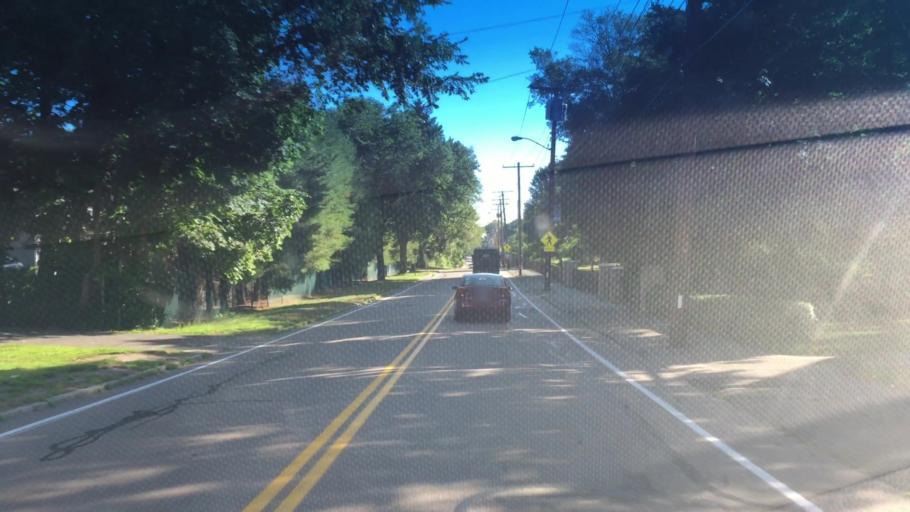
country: US
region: Massachusetts
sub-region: Norfolk County
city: Walpole
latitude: 42.1565
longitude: -71.2206
